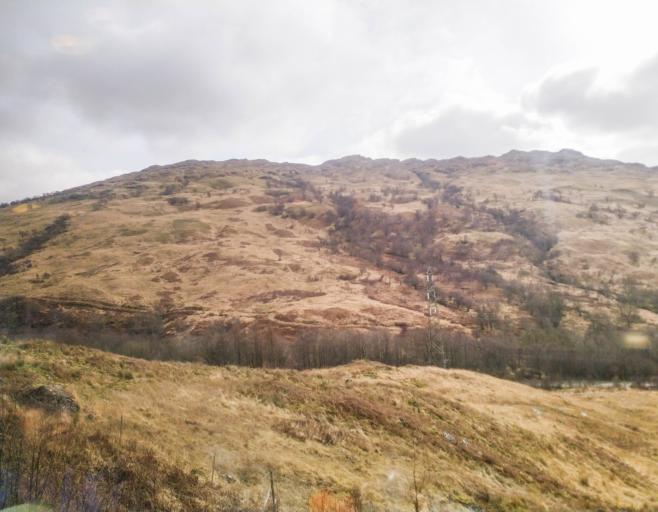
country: GB
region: Scotland
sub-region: Argyll and Bute
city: Garelochhead
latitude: 56.3515
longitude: -4.6982
